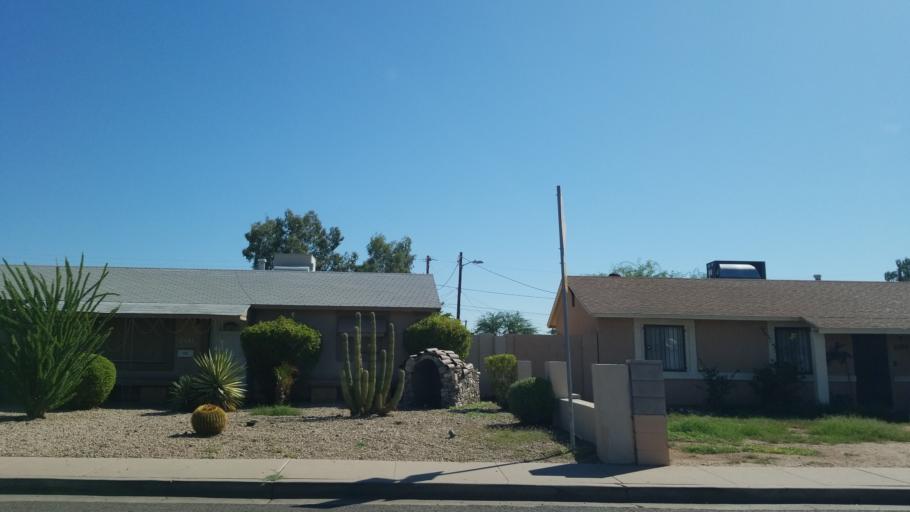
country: US
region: Arizona
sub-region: Maricopa County
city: Glendale
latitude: 33.4819
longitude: -112.1595
